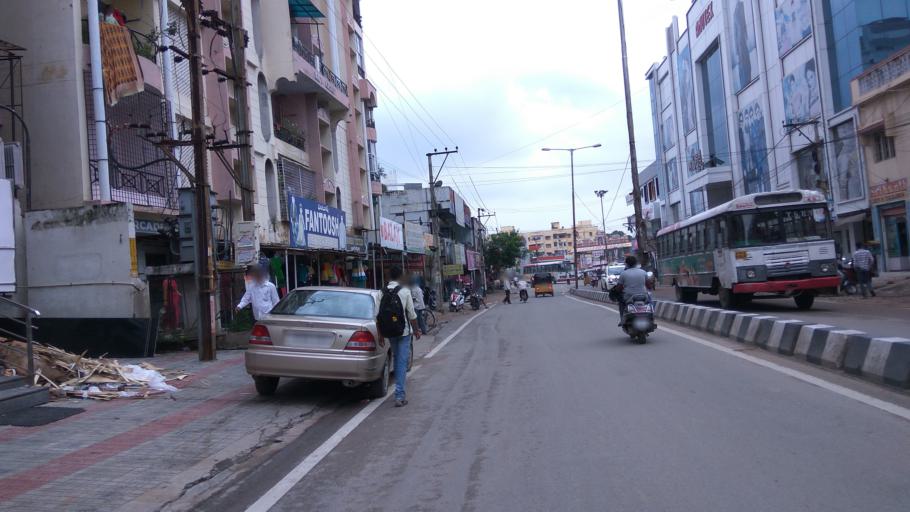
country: IN
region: Telangana
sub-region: Hyderabad
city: Malkajgiri
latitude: 17.4512
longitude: 78.5329
